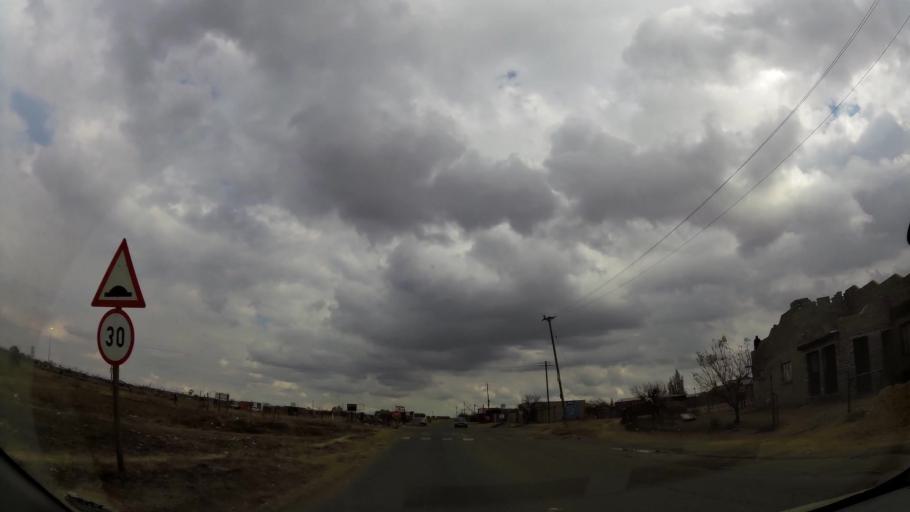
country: ZA
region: Orange Free State
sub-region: Fezile Dabi District Municipality
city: Sasolburg
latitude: -26.8536
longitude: 27.8735
